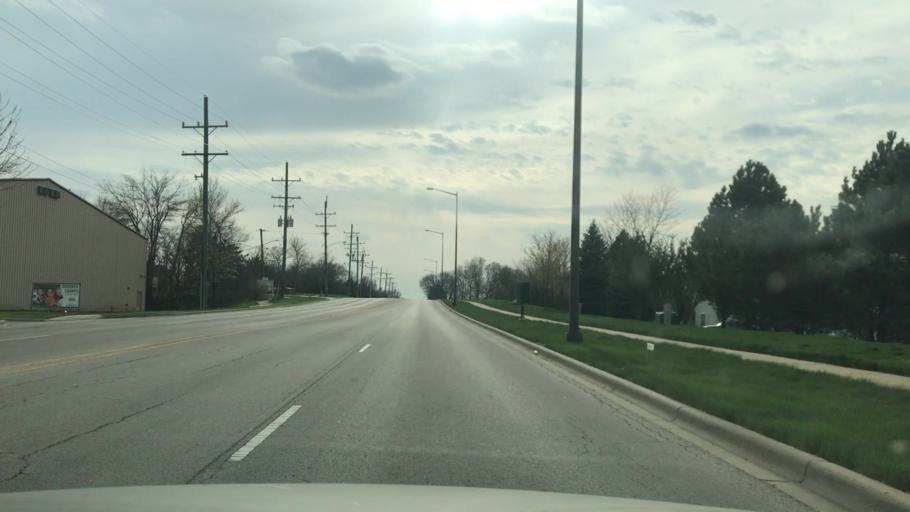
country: US
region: Illinois
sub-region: Kane County
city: Aurora
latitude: 41.7652
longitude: -88.2579
